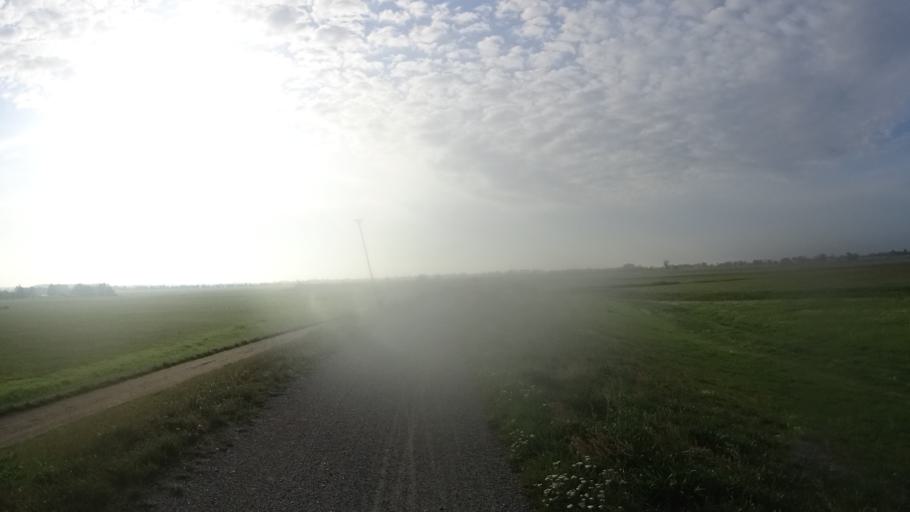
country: DE
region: Brandenburg
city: Lanz
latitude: 53.0574
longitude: 11.5566
